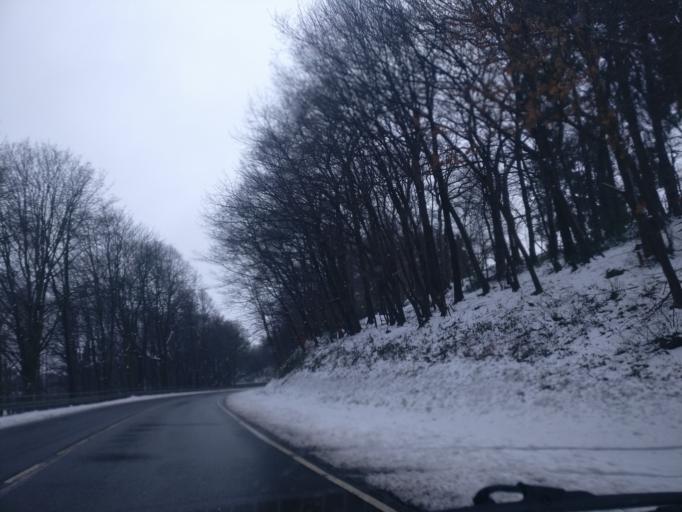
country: DE
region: North Rhine-Westphalia
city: Huckeswagen
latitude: 51.1882
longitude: 7.2811
